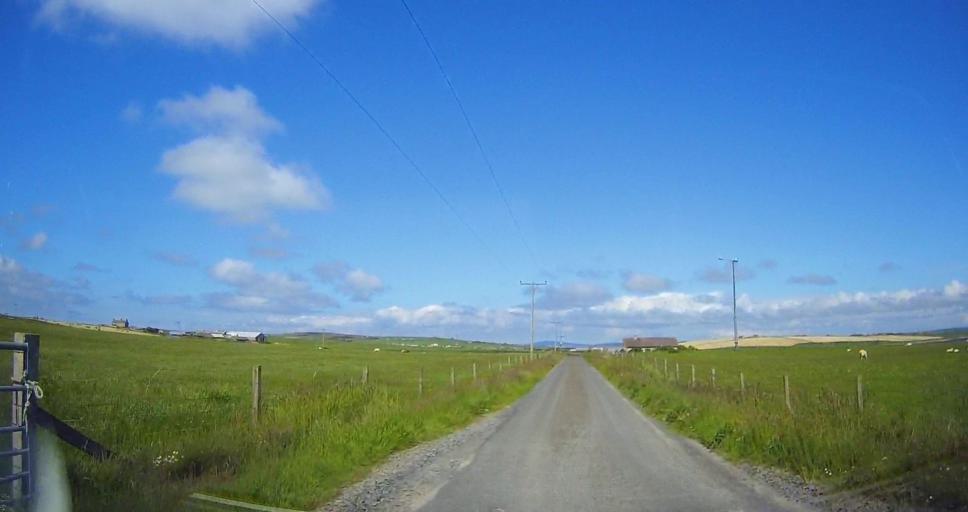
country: GB
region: Scotland
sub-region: Orkney Islands
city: Kirkwall
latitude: 58.8301
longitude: -2.8975
